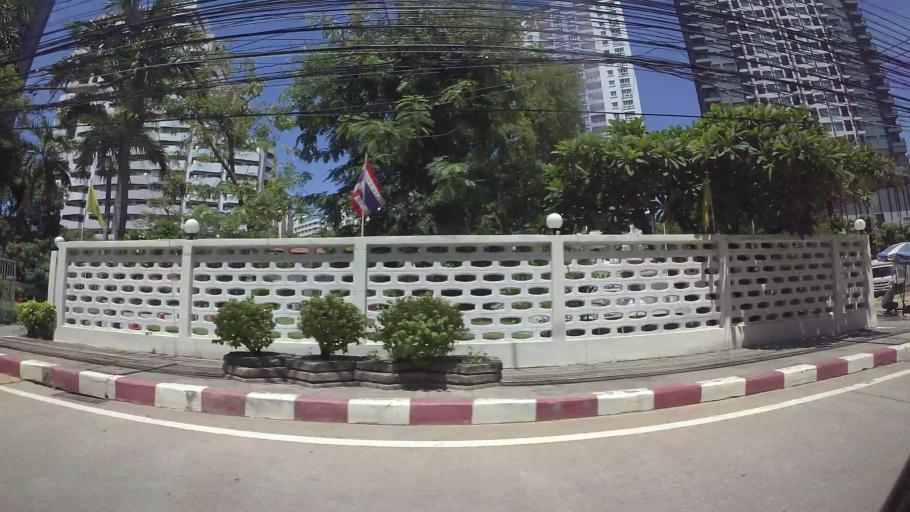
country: TH
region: Chon Buri
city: Si Racha
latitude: 13.1695
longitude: 100.9258
